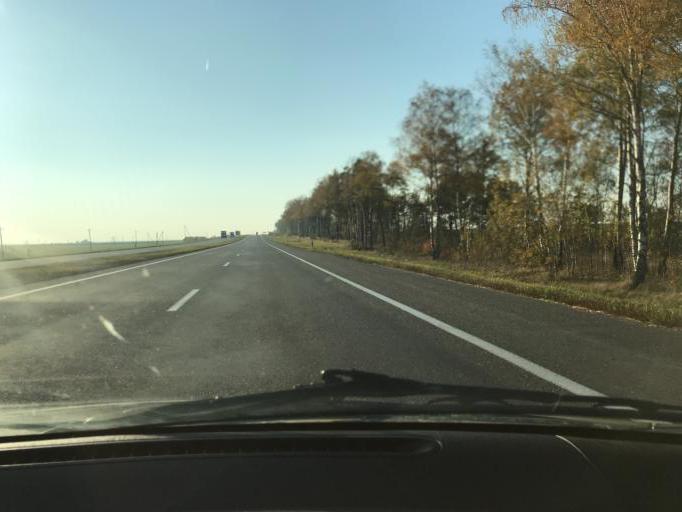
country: BY
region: Minsk
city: Loshnitsa
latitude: 54.2908
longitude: 28.8480
